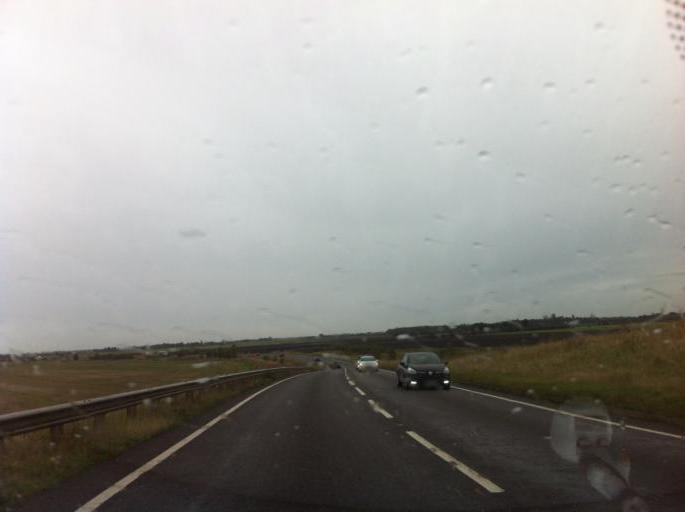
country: GB
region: England
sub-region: Peterborough
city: Eye
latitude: 52.6143
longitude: -0.2108
